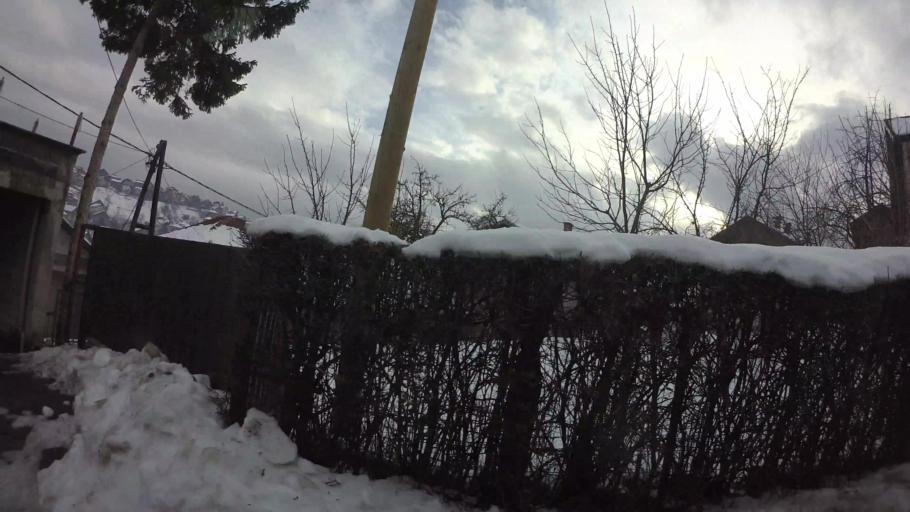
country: BA
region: Federation of Bosnia and Herzegovina
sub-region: Kanton Sarajevo
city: Sarajevo
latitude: 43.8595
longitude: 18.3461
